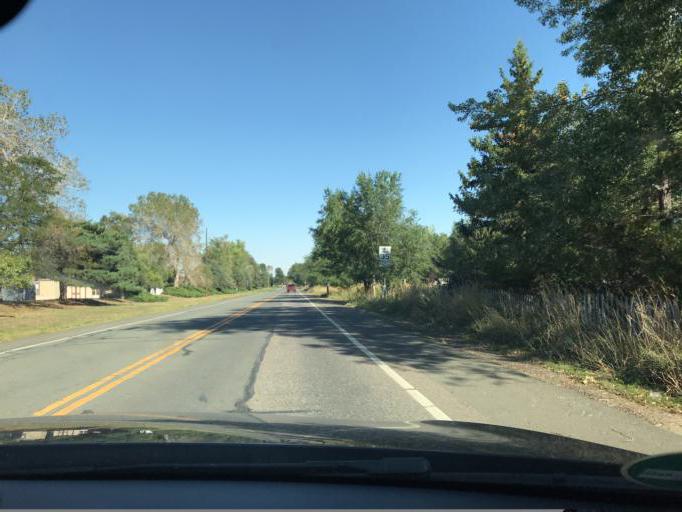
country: US
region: Colorado
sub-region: Boulder County
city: Boulder
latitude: 40.0547
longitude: -105.2717
